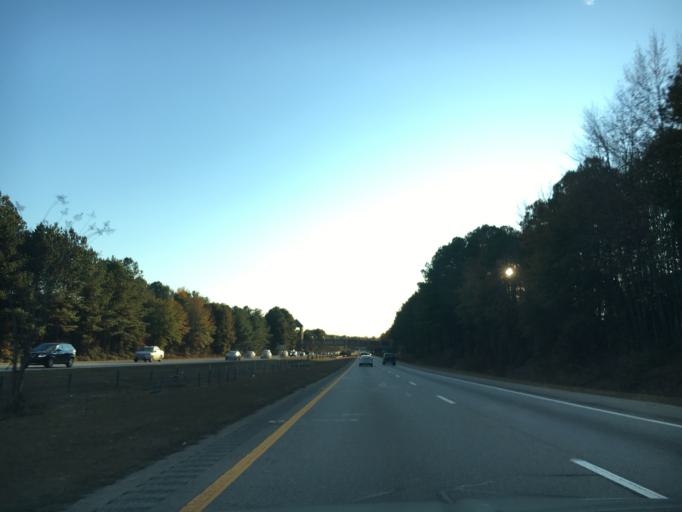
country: US
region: South Carolina
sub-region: Richland County
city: Forest Acres
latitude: 34.0449
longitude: -81.0124
